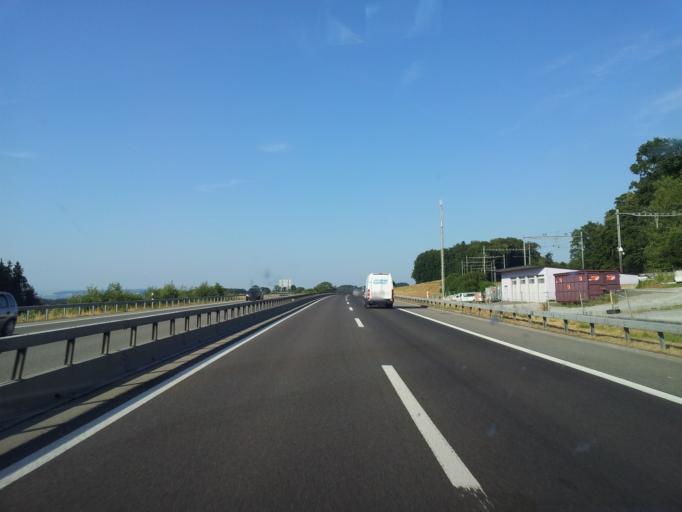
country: CH
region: Fribourg
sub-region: Sense District
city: Dudingen
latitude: 46.8618
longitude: 7.2033
